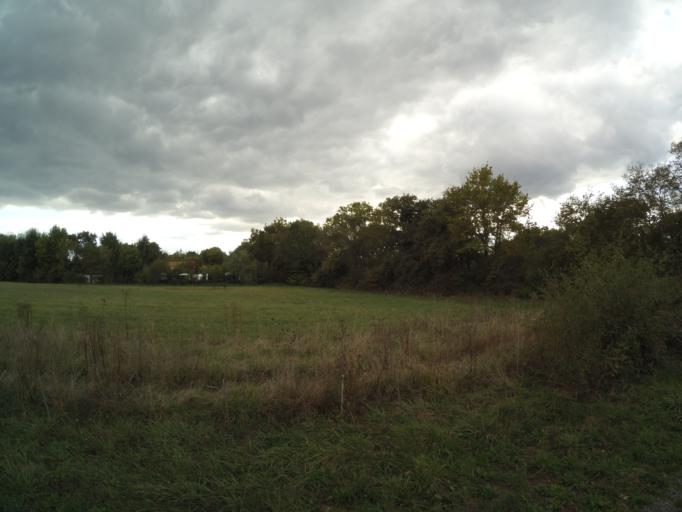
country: FR
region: Pays de la Loire
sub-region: Departement de la Loire-Atlantique
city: Remouille
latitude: 47.0637
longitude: -1.3716
